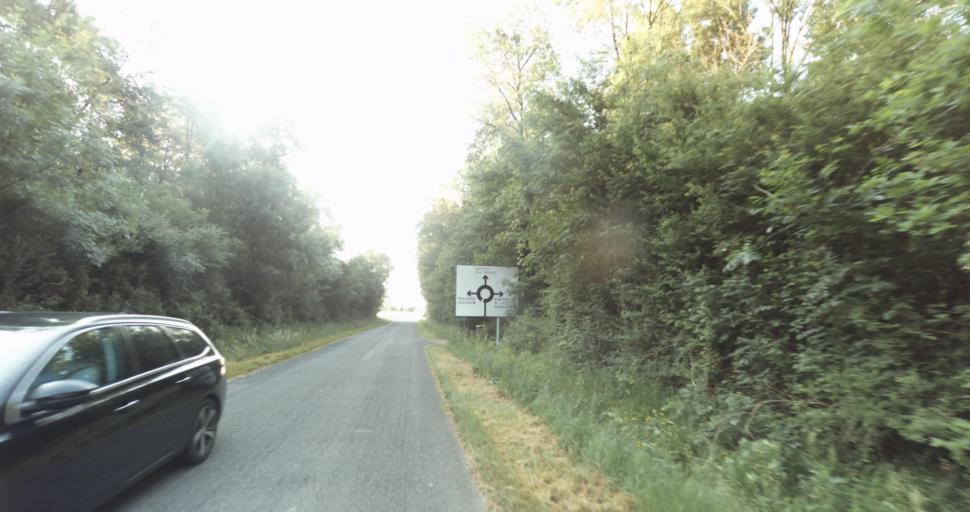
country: FR
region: Midi-Pyrenees
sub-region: Departement de la Haute-Garonne
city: Fontenilles
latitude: 43.5683
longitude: 1.1933
